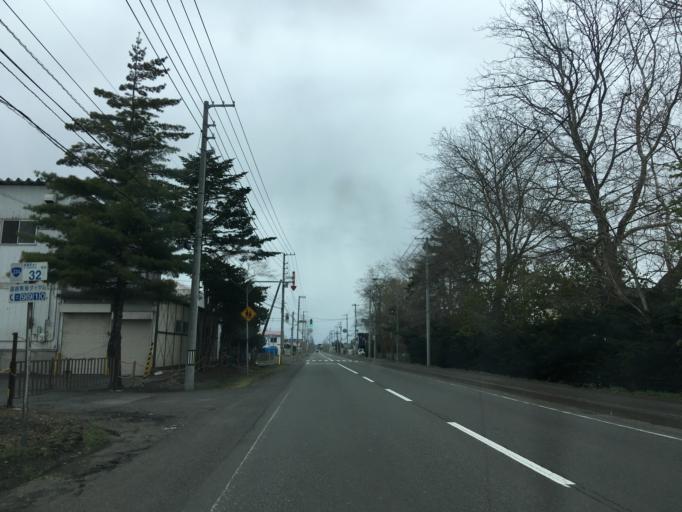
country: JP
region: Hokkaido
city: Chitose
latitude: 42.9409
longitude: 141.8045
